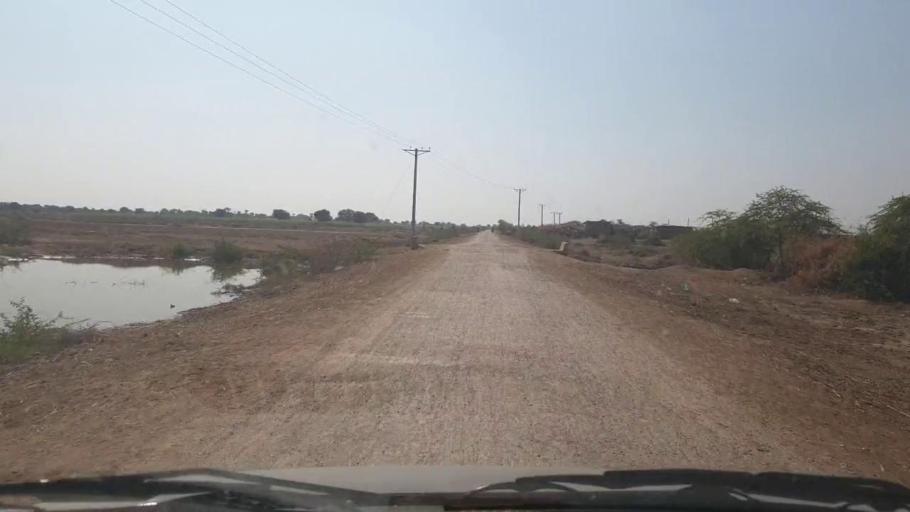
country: PK
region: Sindh
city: Samaro
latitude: 25.2287
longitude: 69.3355
